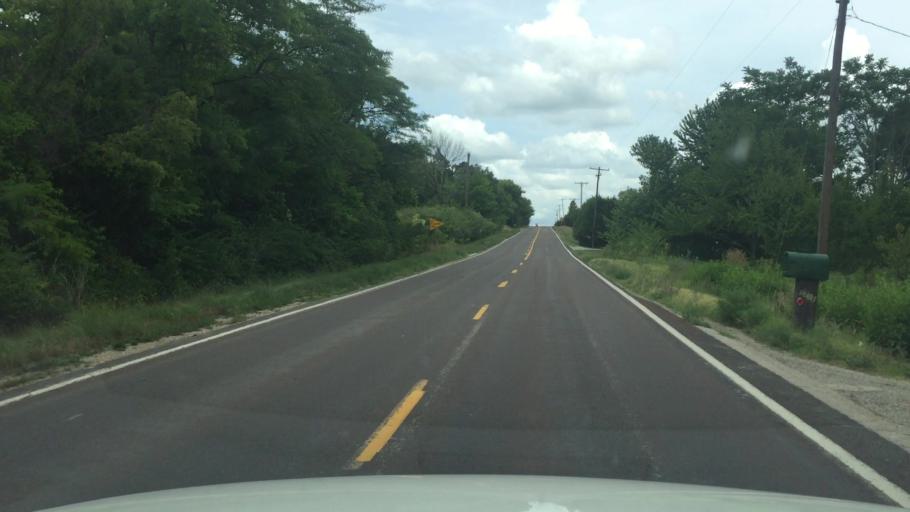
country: US
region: Kansas
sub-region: Shawnee County
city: Topeka
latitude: 39.0294
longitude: -95.5160
